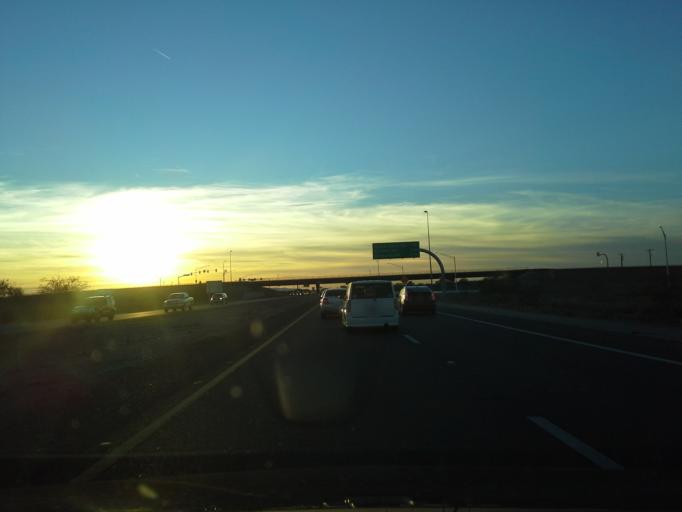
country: US
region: Arizona
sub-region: Pinal County
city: Apache Junction
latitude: 33.3867
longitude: -111.5770
